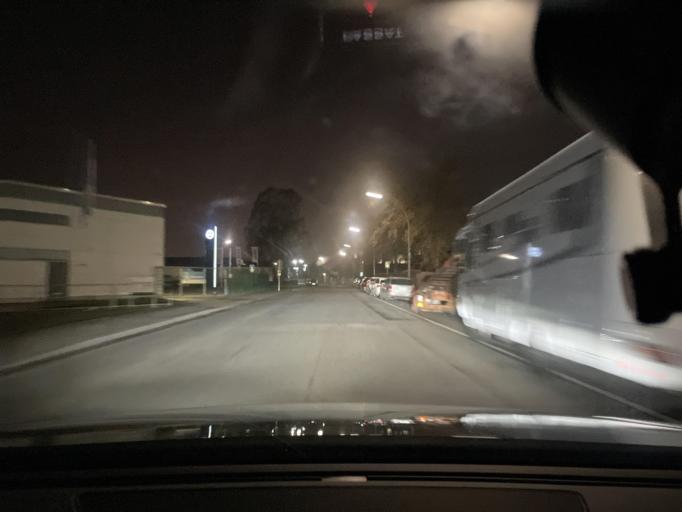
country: DE
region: North Rhine-Westphalia
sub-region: Regierungsbezirk Dusseldorf
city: Korschenbroich
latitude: 51.2308
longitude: 6.4792
